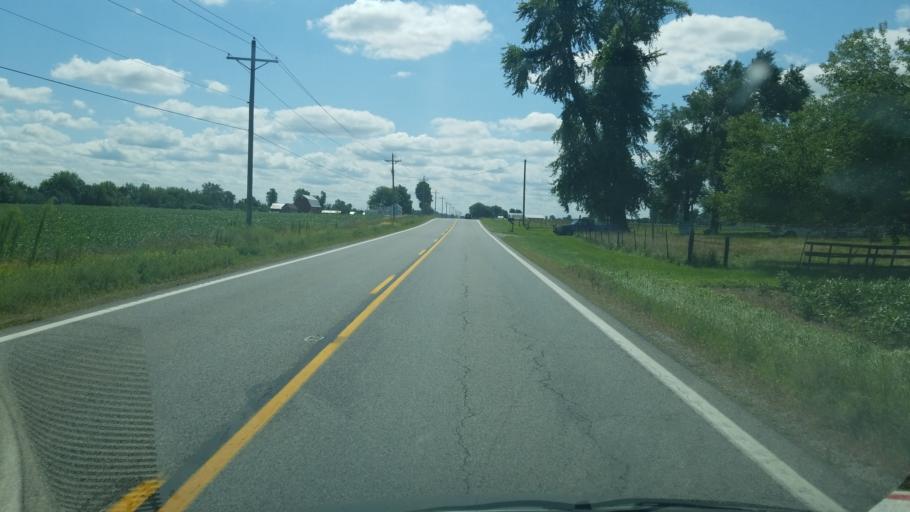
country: US
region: Ohio
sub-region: Fulton County
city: Delta
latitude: 41.6371
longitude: -84.0348
